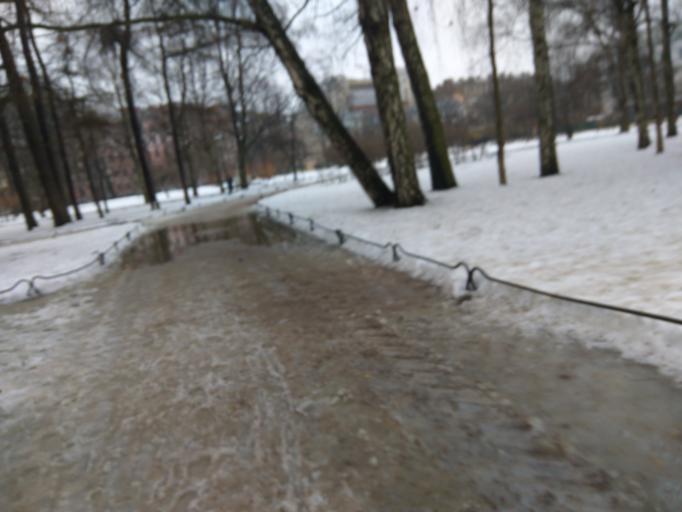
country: RU
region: St.-Petersburg
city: Centralniy
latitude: 59.9445
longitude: 30.3703
